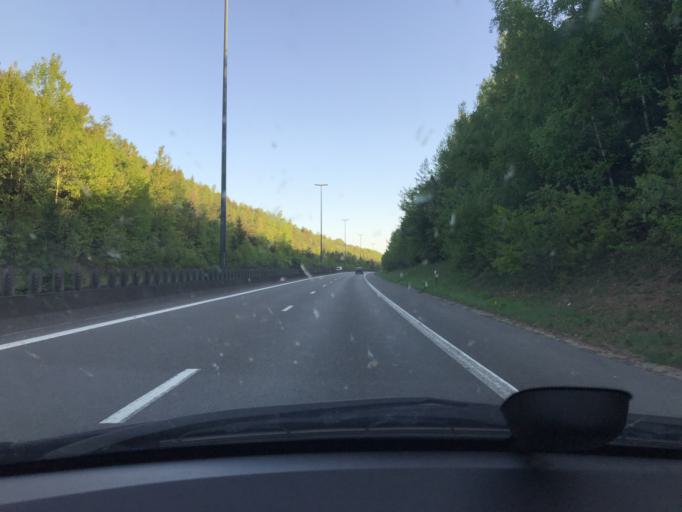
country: BE
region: Wallonia
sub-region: Province du Luxembourg
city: Tellin
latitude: 50.0499
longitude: 5.2111
